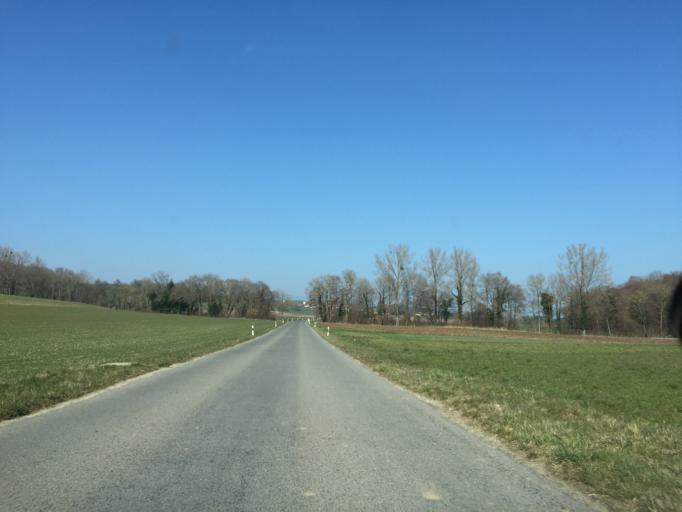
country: CH
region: Vaud
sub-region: Morges District
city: La Chaux
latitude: 46.6289
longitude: 6.4737
